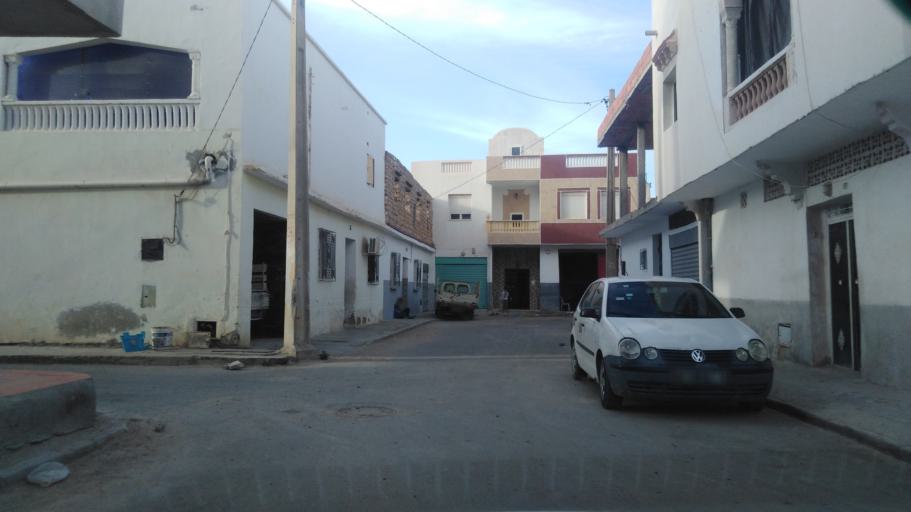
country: TN
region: Tataouine
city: Tataouine
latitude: 32.9386
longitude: 10.4542
